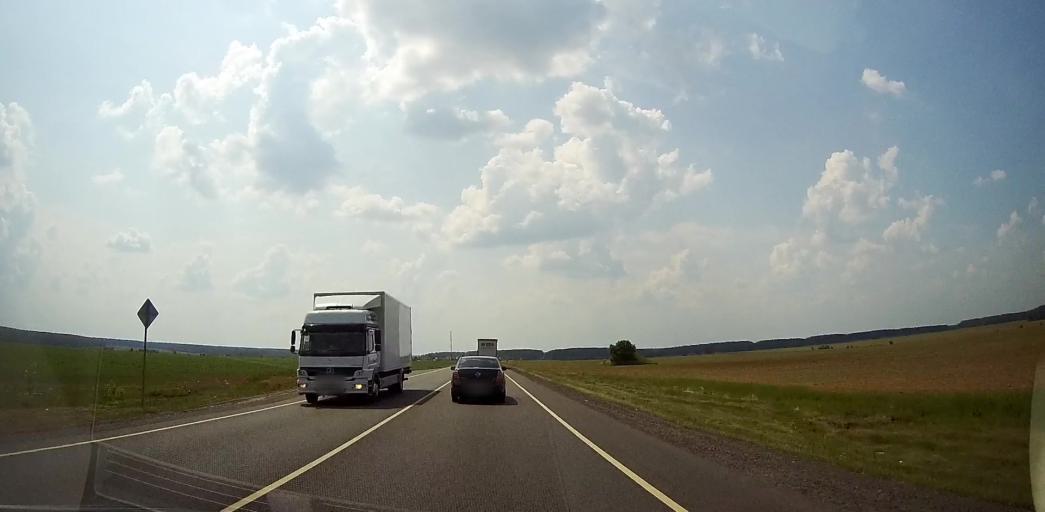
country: RU
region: Moskovskaya
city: Malino
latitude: 55.1314
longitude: 38.2534
